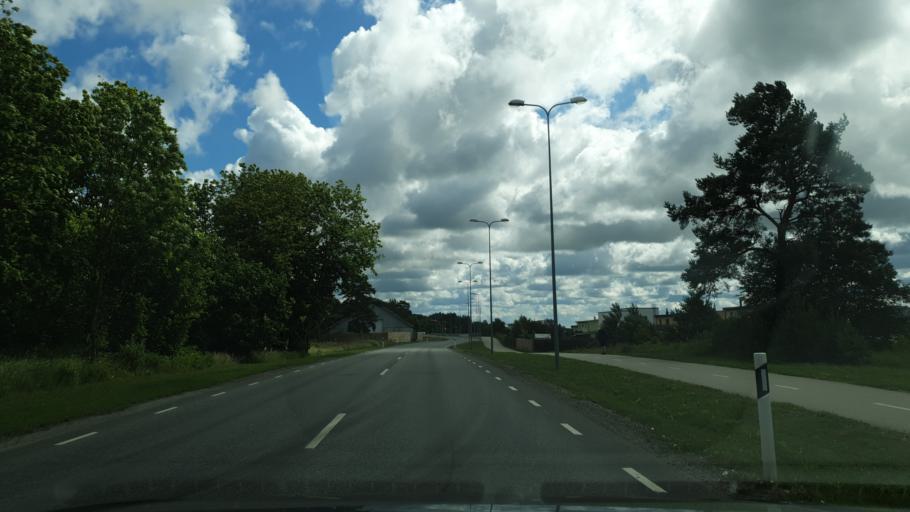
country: EE
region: Harju
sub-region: Viimsi vald
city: Viimsi
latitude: 59.5072
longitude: 24.8610
